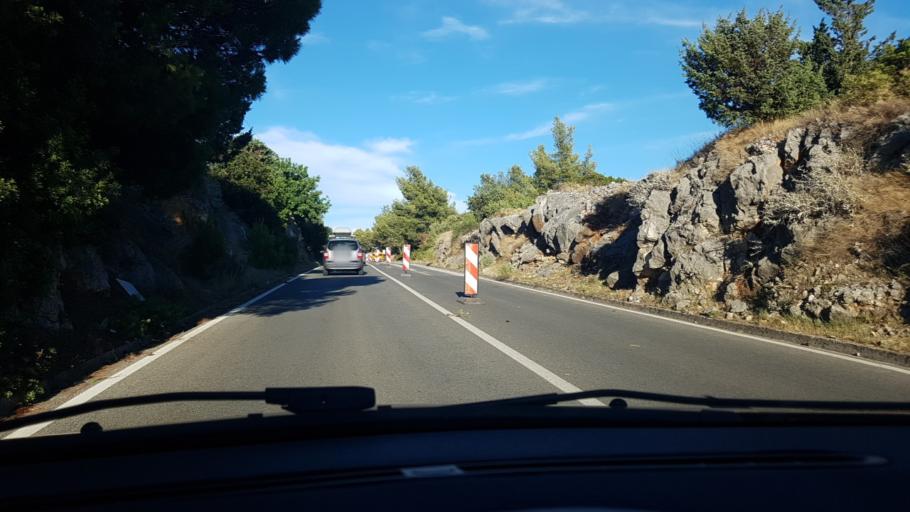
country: HR
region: Splitsko-Dalmatinska
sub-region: Grad Trogir
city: Trogir
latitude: 43.5147
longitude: 16.2009
